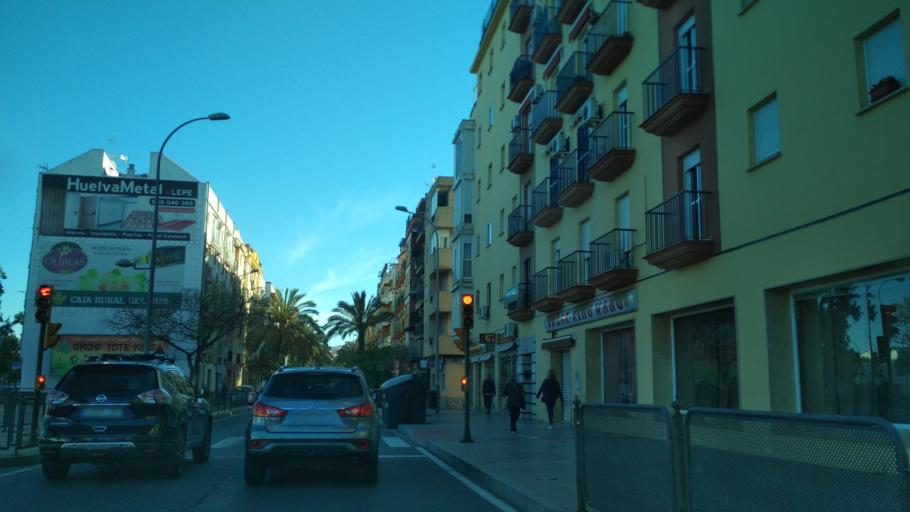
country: ES
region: Andalusia
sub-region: Provincia de Huelva
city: Huelva
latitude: 37.2688
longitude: -6.9515
